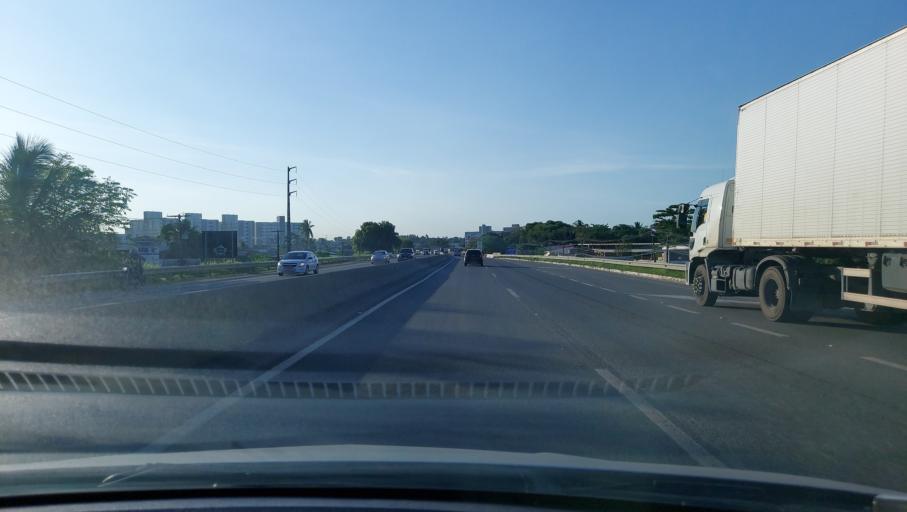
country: BR
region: Bahia
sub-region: Lauro De Freitas
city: Lauro de Freitas
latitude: -12.9056
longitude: -38.3536
